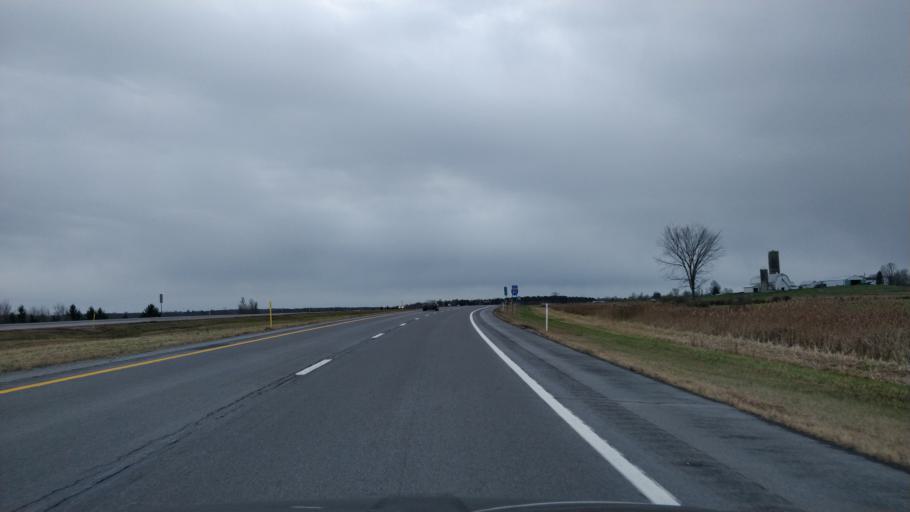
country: US
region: New York
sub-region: Jefferson County
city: Calcium
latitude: 44.1573
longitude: -75.8799
